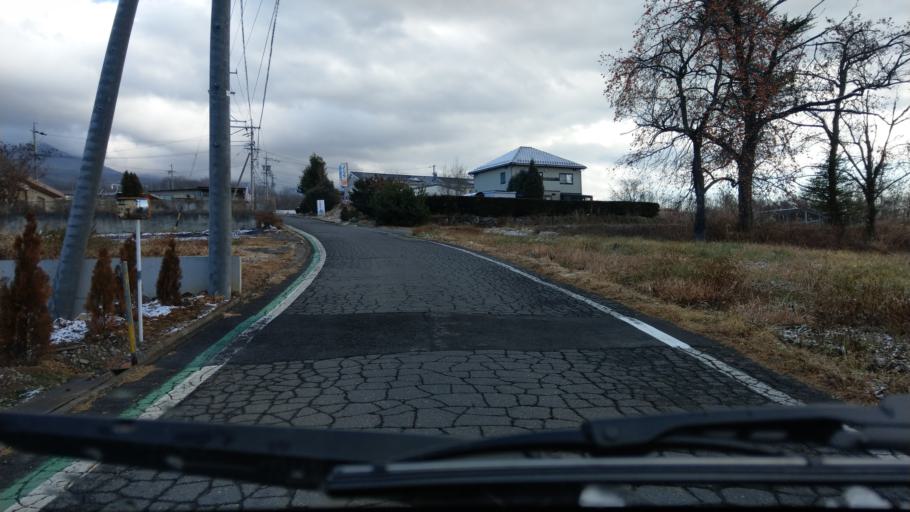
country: JP
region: Nagano
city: Komoro
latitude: 36.3508
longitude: 138.3988
